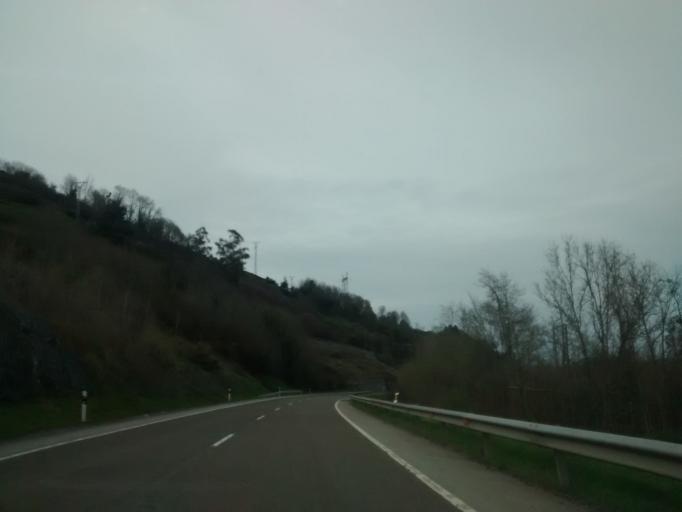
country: ES
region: Cantabria
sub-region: Provincia de Cantabria
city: Santiurde de Toranzo
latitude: 43.2260
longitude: -3.9461
